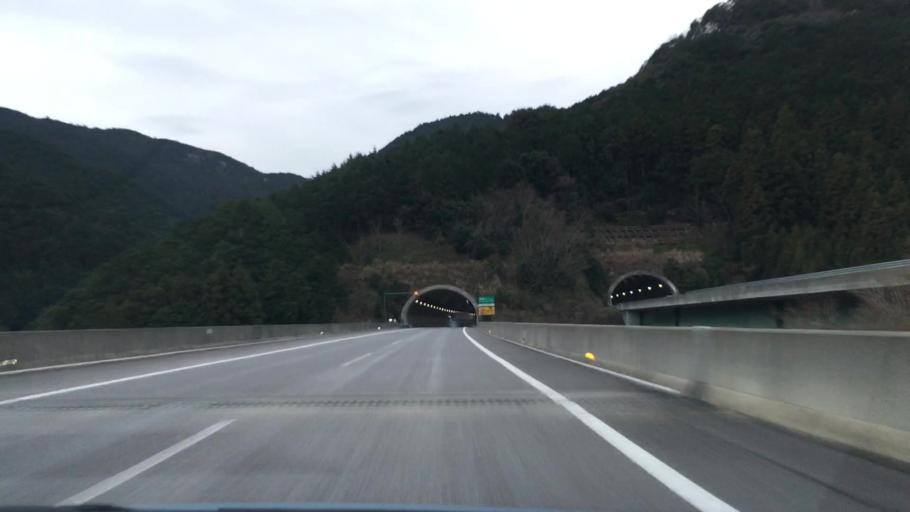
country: JP
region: Aichi
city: Shinshiro
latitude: 34.8380
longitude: 137.5997
